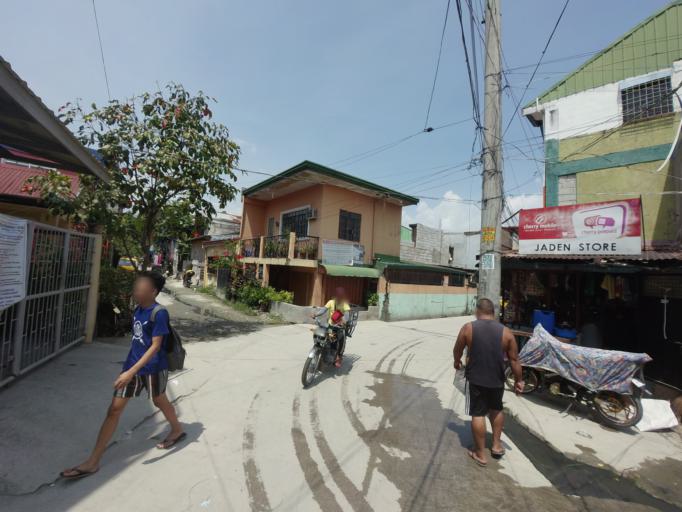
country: PH
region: Calabarzon
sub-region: Province of Rizal
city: Taytay
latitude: 14.5416
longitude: 121.1085
